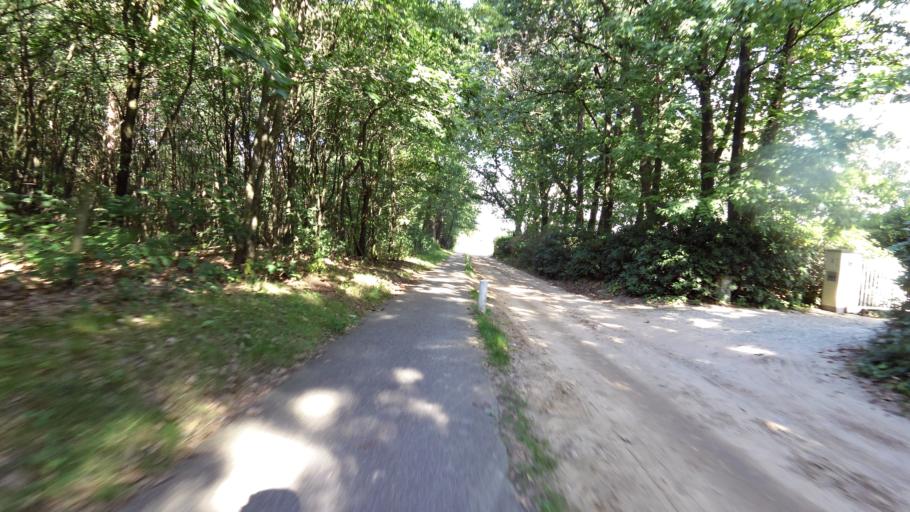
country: NL
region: Gelderland
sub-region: Gemeente Renkum
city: Renkum
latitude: 52.0122
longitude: 5.7156
